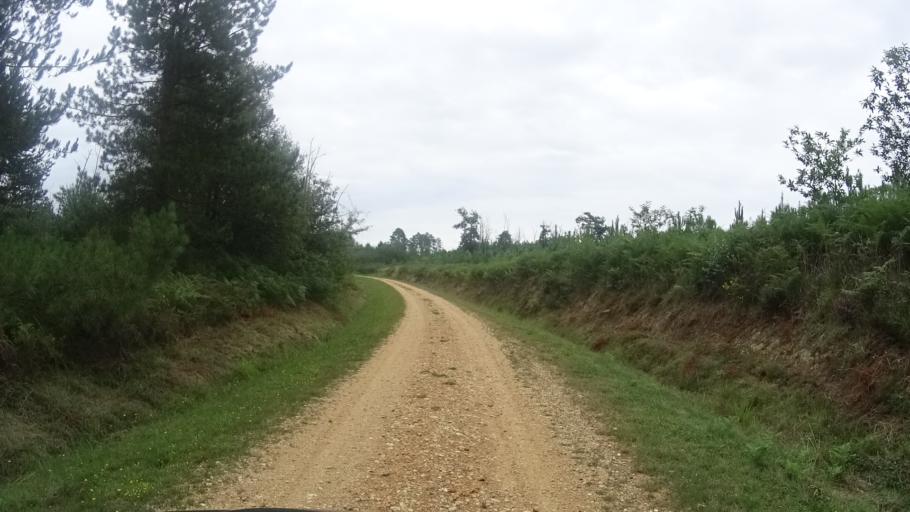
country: FR
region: Aquitaine
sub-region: Departement de la Dordogne
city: Sourzac
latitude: 45.0335
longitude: 0.4051
